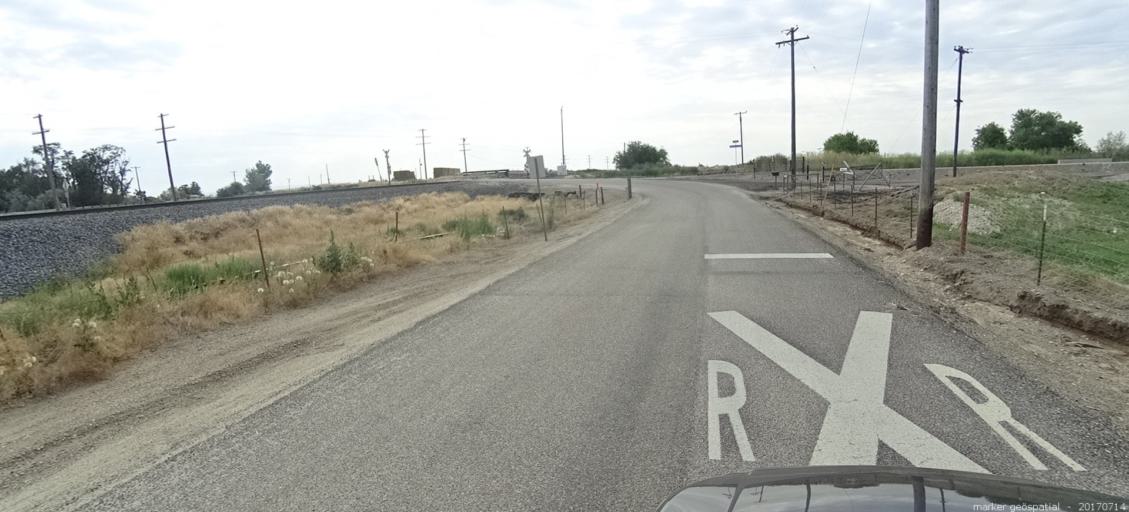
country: US
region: Idaho
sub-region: Ada County
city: Kuna
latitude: 43.4588
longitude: -116.3552
